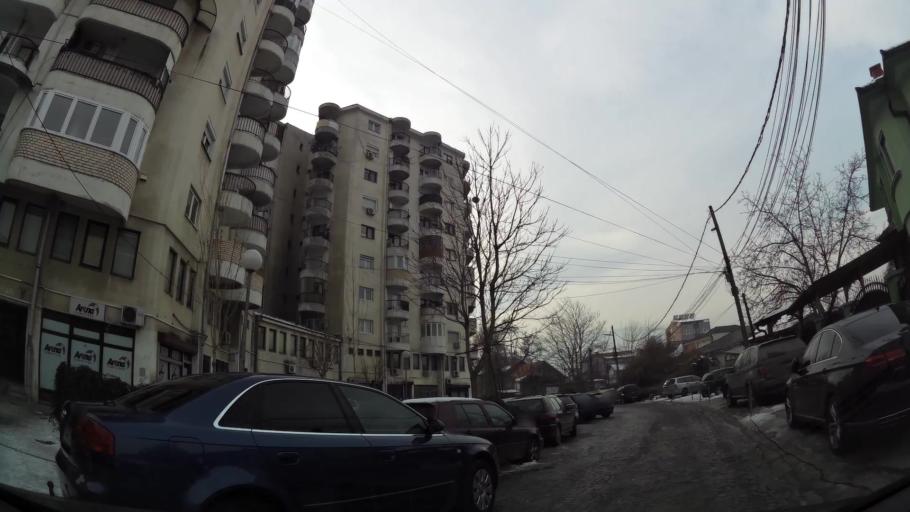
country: MK
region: Cair
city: Cair
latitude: 42.0092
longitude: 21.4424
